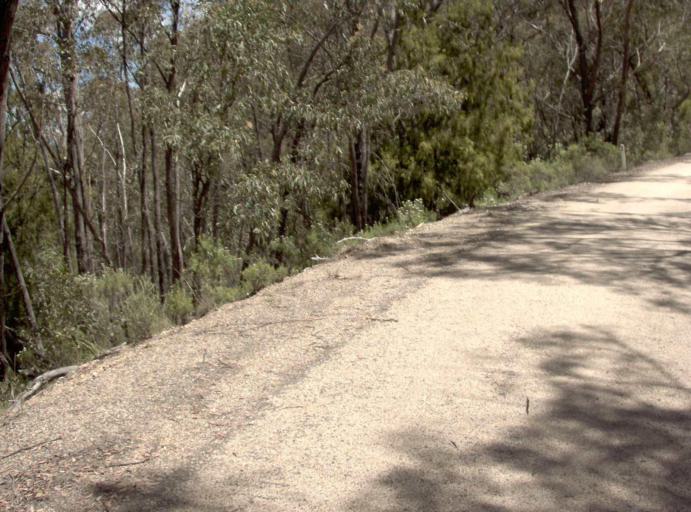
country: AU
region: New South Wales
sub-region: Snowy River
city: Jindabyne
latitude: -37.0841
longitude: 148.3329
